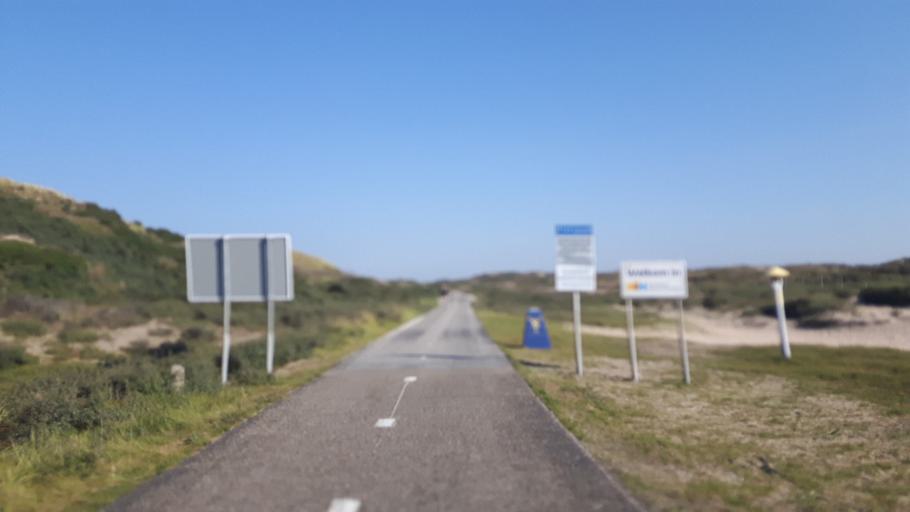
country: NL
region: North Holland
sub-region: Gemeente Zandvoort
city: Zandvoort
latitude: 52.3273
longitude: 4.4970
